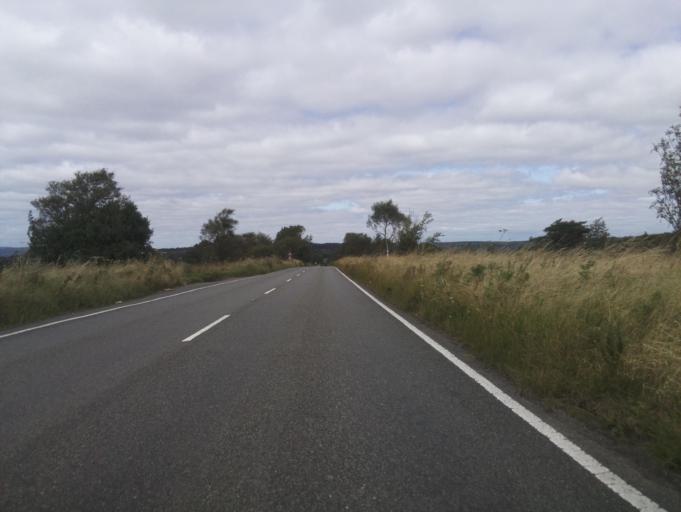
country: GB
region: England
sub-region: Devon
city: Bishopsteignton
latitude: 50.5796
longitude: -3.5304
